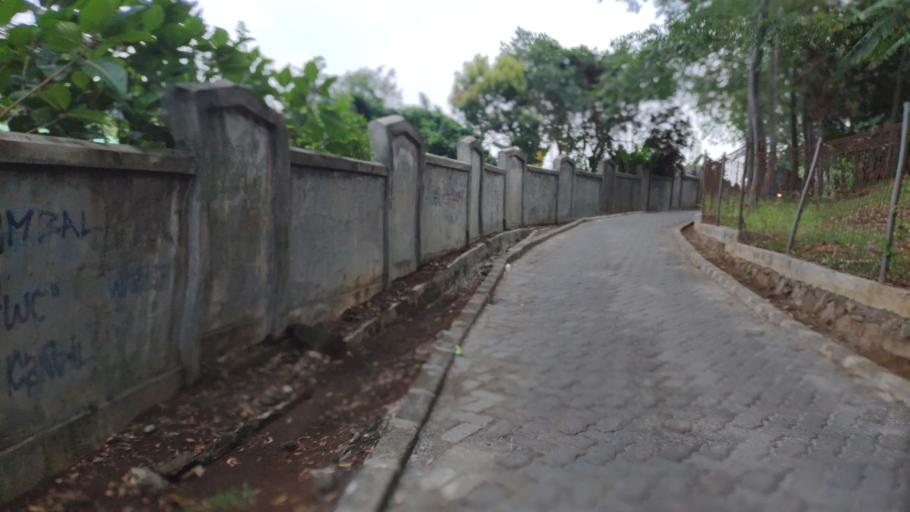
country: ID
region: West Java
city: Pamulang
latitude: -6.3060
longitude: 106.8239
